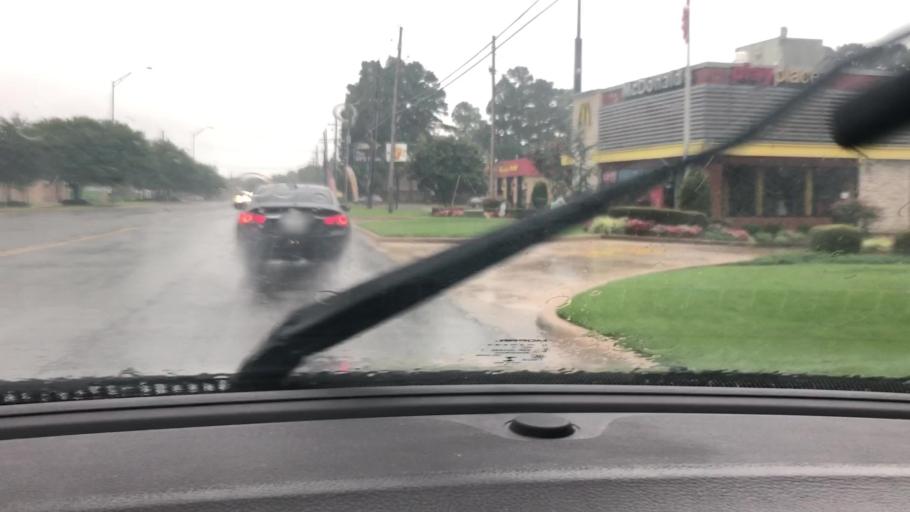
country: US
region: Texas
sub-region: Bowie County
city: Wake Village
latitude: 33.4534
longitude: -94.0826
